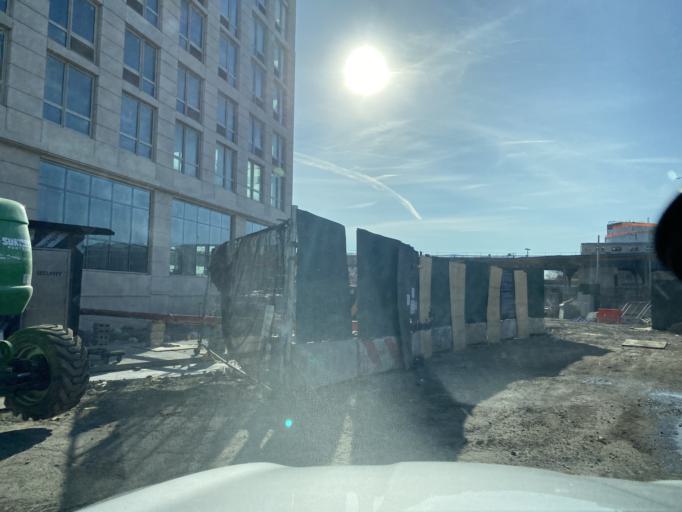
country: US
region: New York
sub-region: Queens County
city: Long Island City
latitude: 40.7446
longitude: -73.9459
